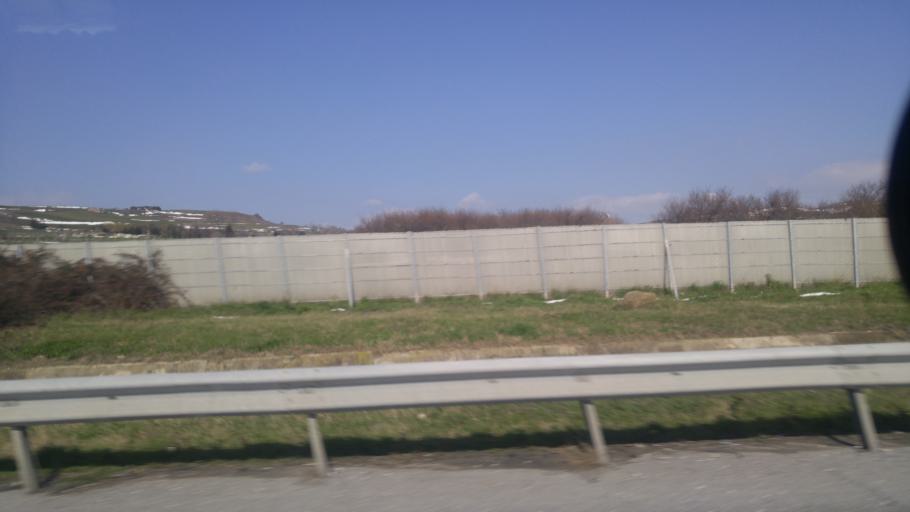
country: TR
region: Istanbul
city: Celaliye
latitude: 41.0667
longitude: 28.3964
